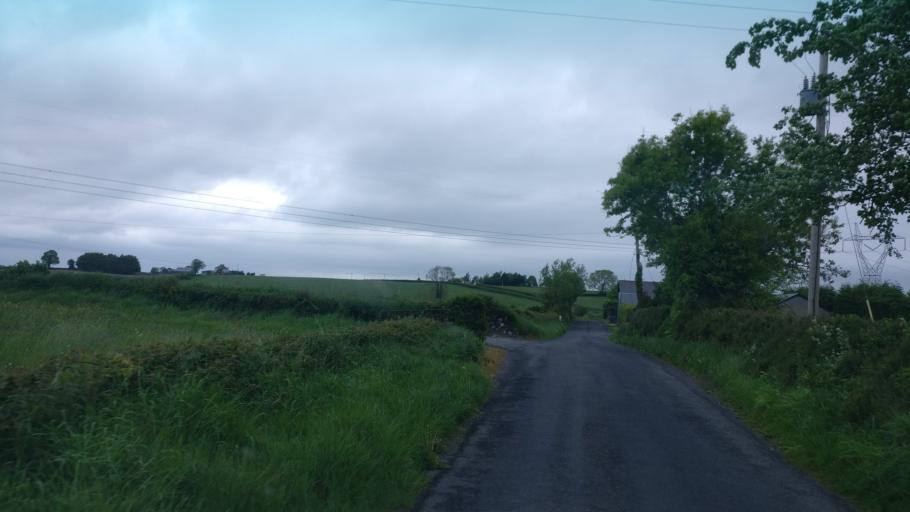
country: IE
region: Connaught
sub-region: County Galway
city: Portumna
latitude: 53.1266
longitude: -8.2901
